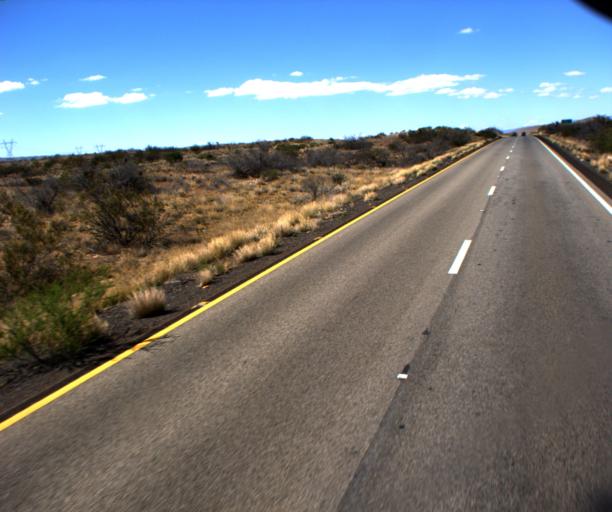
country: US
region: Arizona
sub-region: Mohave County
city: Kingman
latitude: 34.9757
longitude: -113.6687
